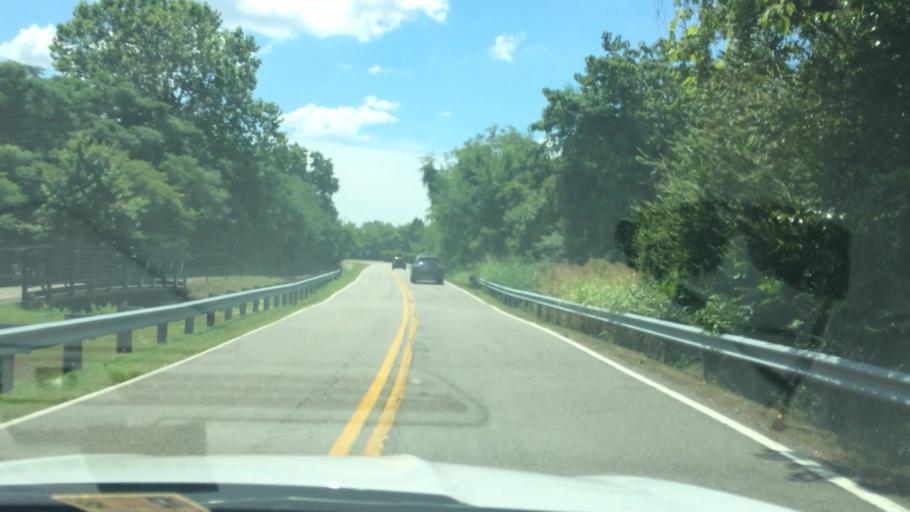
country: US
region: Virginia
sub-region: King William County
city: West Point
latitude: 37.5407
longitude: -76.7945
